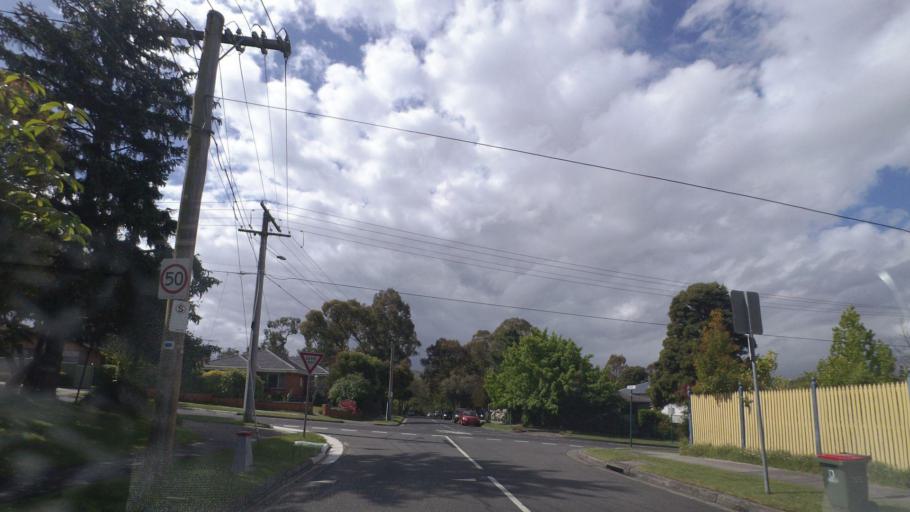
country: AU
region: Victoria
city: Mitcham
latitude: -37.8271
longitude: 145.2049
